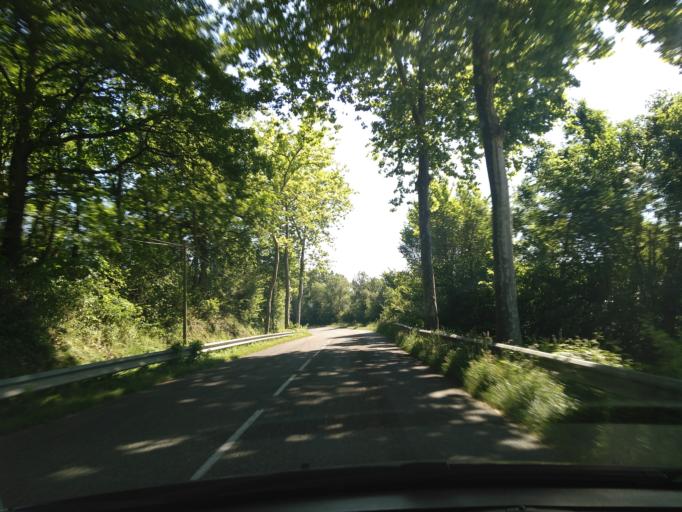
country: FR
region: Midi-Pyrenees
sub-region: Departement du Gers
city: Aubiet
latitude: 43.5330
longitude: 0.7674
